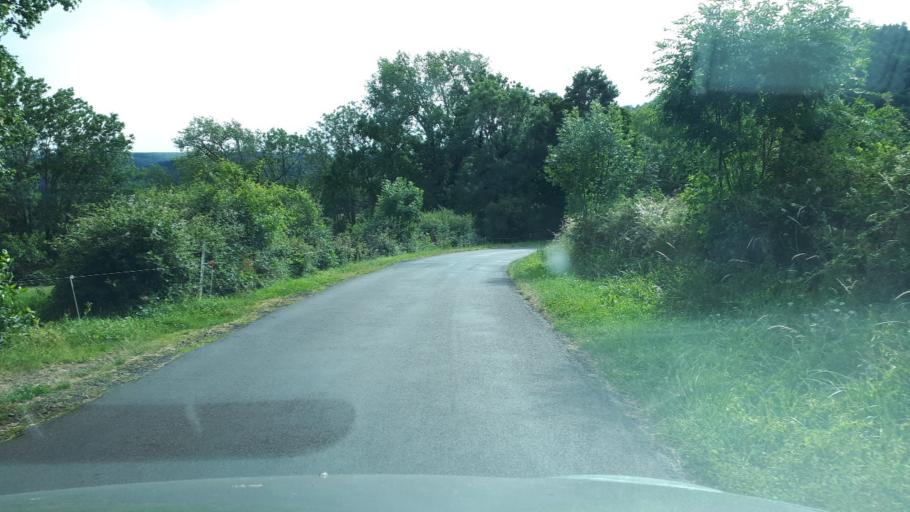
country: FR
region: Auvergne
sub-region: Departement du Puy-de-Dome
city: Aydat
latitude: 45.5919
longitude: 2.9654
